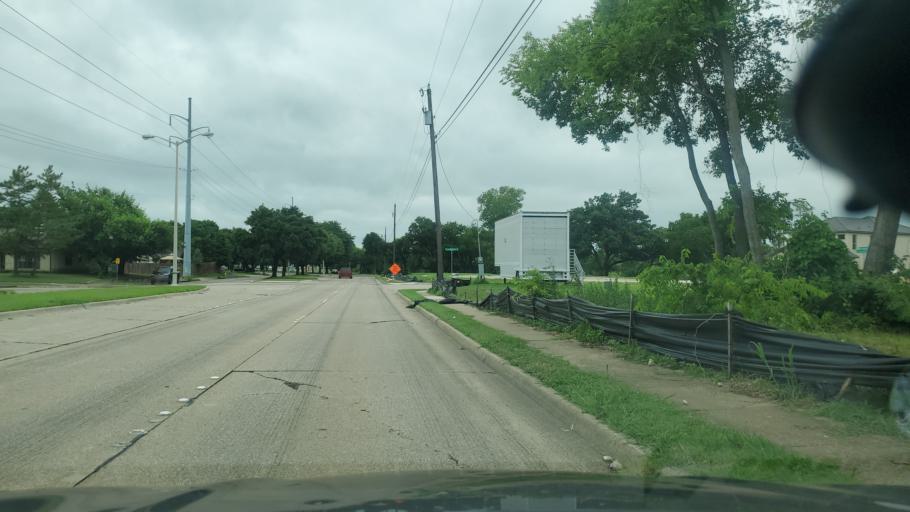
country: US
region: Texas
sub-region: Dallas County
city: Garland
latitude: 32.9340
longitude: -96.6653
